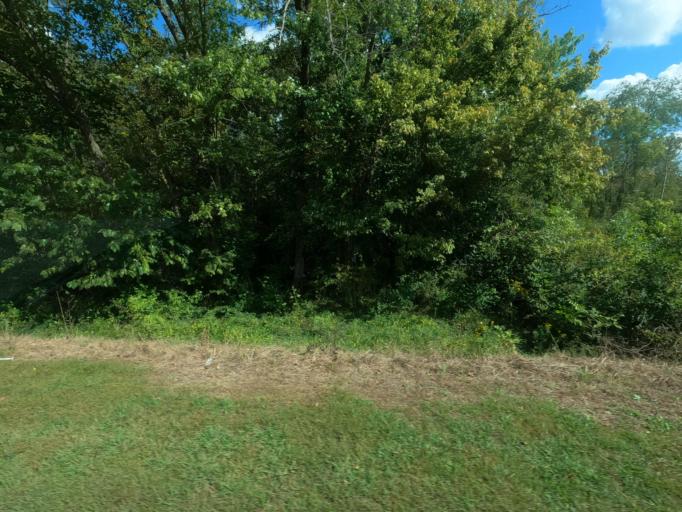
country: US
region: Illinois
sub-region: Johnson County
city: Vienna
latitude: 37.4191
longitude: -88.8931
